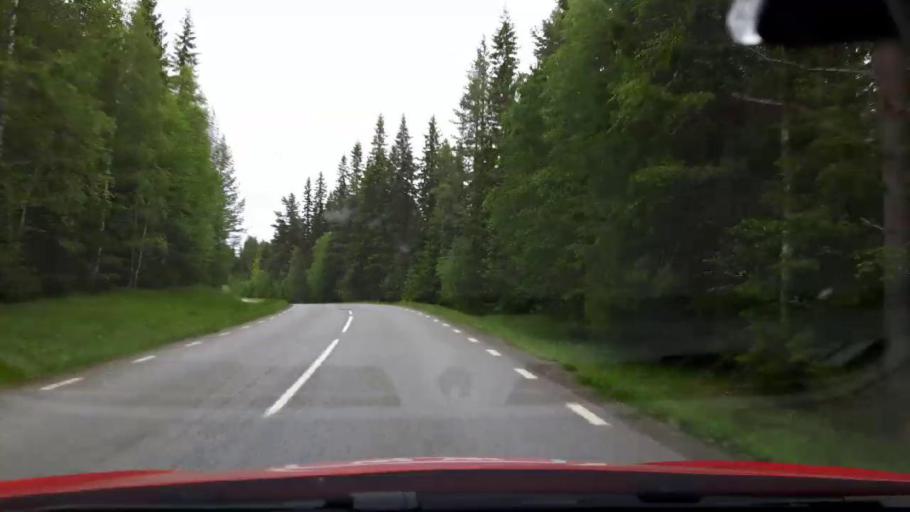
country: SE
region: Jaemtland
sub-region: Stroemsunds Kommun
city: Stroemsund
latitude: 63.4483
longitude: 15.4707
